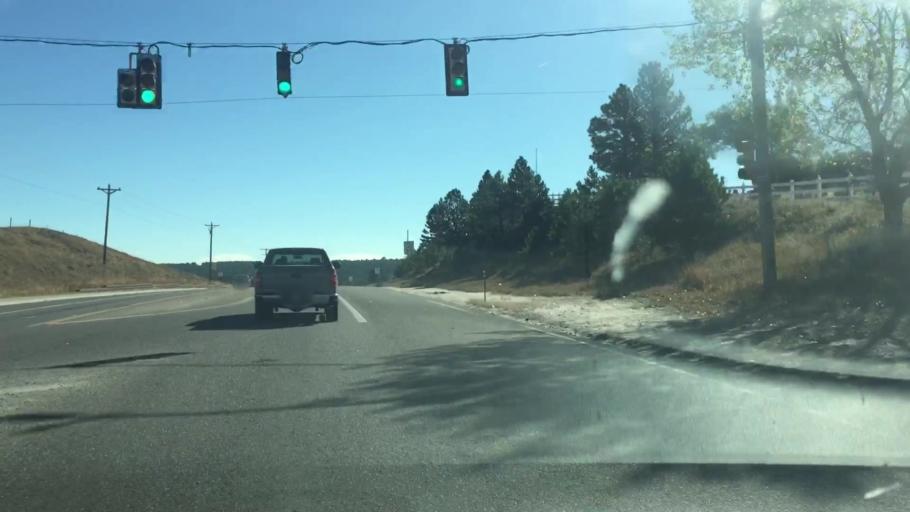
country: US
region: Colorado
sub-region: Elbert County
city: Elizabeth
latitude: 39.3616
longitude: -104.6069
